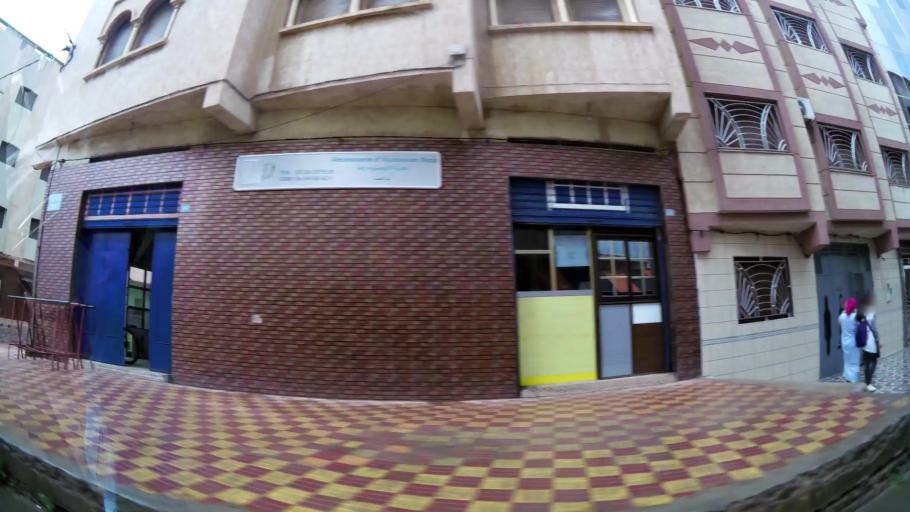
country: MA
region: Oriental
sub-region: Nador
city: Nador
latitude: 35.1714
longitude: -2.9398
